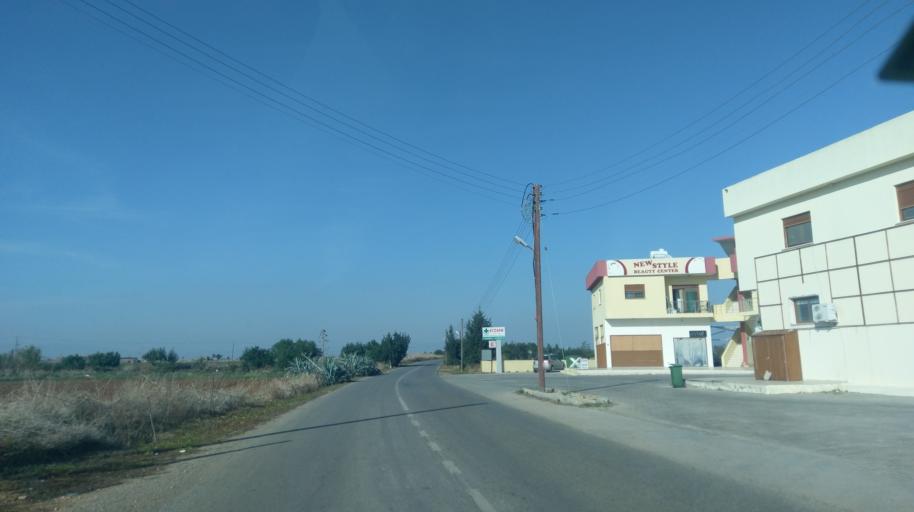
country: CY
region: Larnaka
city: Pergamos
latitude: 35.0538
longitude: 33.7106
